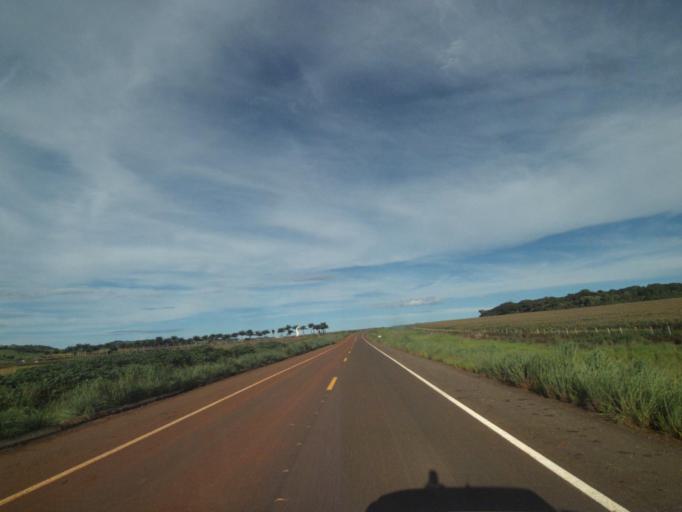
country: BR
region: Goias
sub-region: Jaragua
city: Jaragua
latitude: -15.9032
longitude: -49.5415
